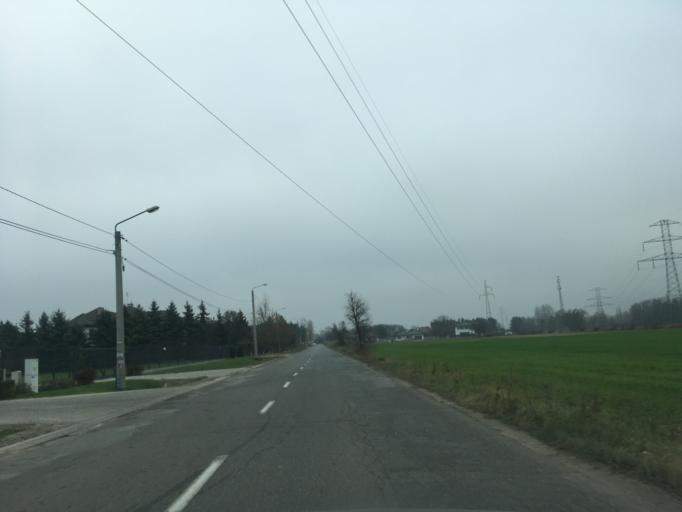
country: PL
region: Masovian Voivodeship
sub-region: Powiat piaseczynski
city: Lesznowola
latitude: 52.0793
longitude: 20.9672
